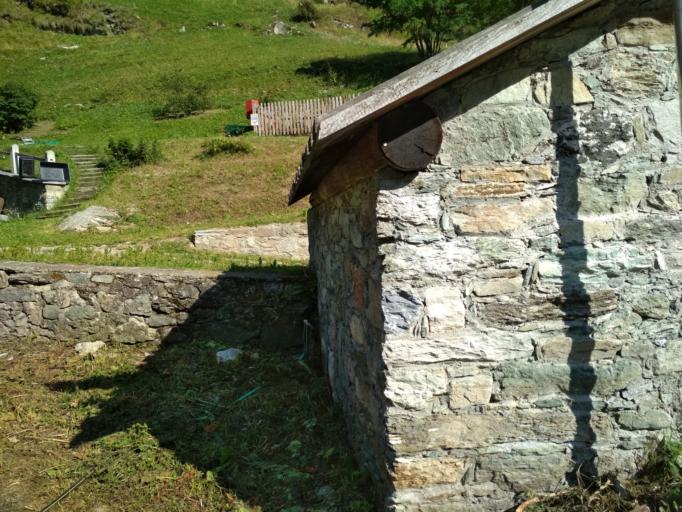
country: IT
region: Aosta Valley
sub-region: Valle d'Aosta
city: Gressoney-Saint-Jean
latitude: 45.7993
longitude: 7.8259
